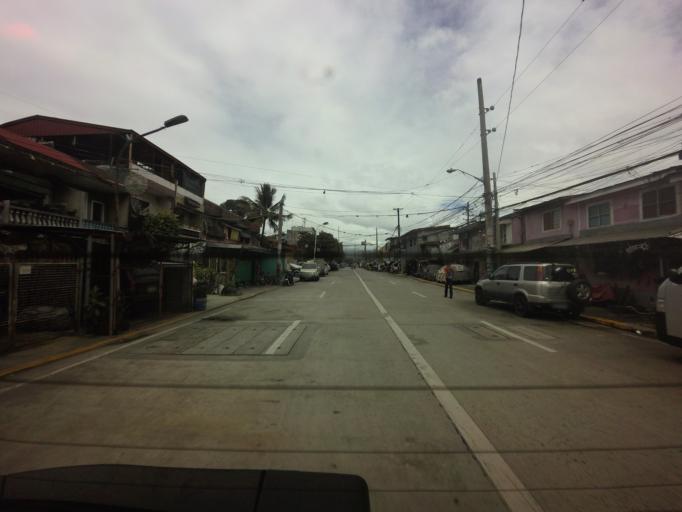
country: PH
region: Metro Manila
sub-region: City of Manila
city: Manila
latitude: 14.6183
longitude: 120.9741
